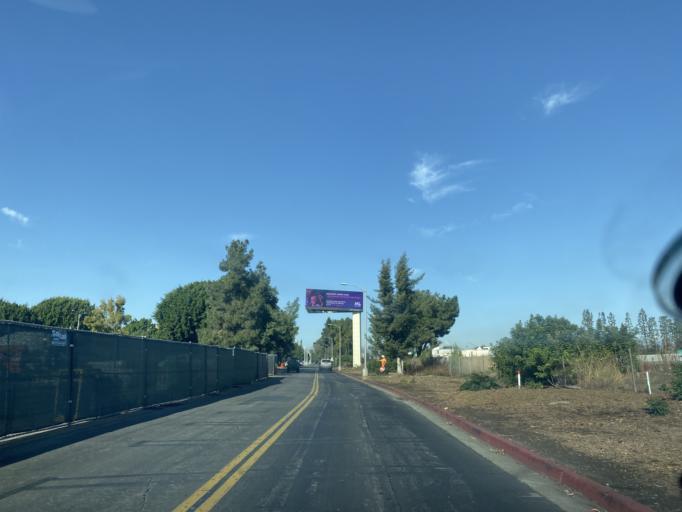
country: US
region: California
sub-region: Orange County
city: Placentia
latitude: 33.8814
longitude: -117.8811
